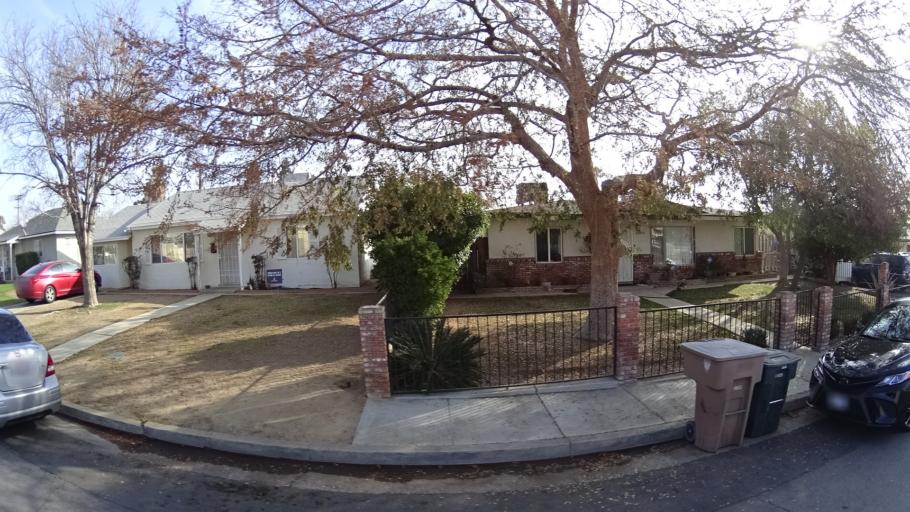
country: US
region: California
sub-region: Kern County
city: Oildale
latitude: 35.3987
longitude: -118.9830
